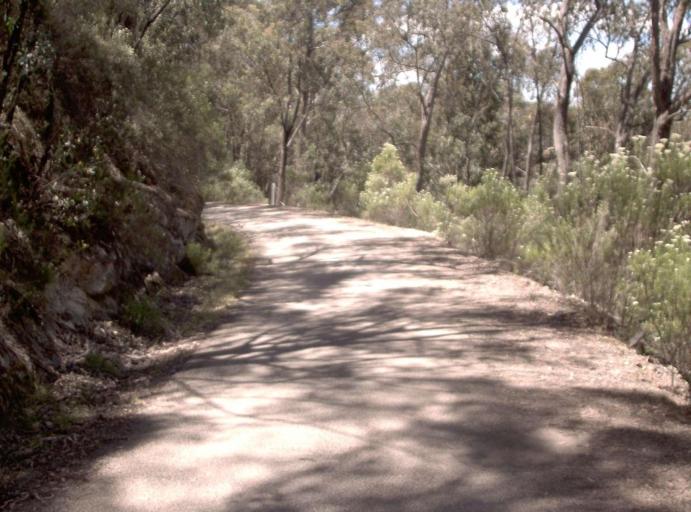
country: AU
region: New South Wales
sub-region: Snowy River
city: Jindabyne
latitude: -37.0829
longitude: 148.3340
